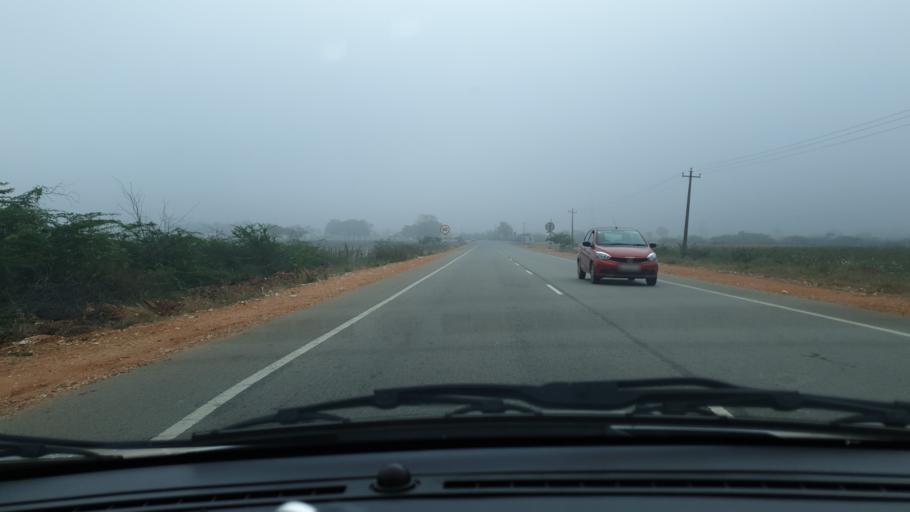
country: IN
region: Telangana
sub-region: Nalgonda
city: Devarkonda
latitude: 16.6319
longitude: 78.6075
